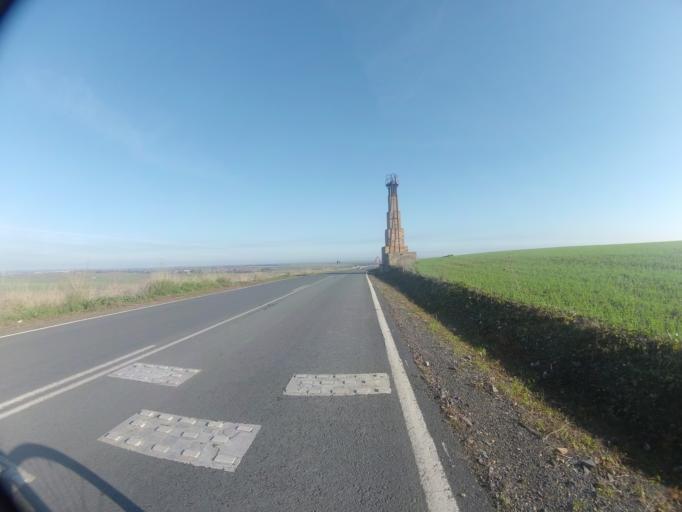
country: ES
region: Andalusia
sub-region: Provincia de Huelva
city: Huelva
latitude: 37.3046
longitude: -6.9236
